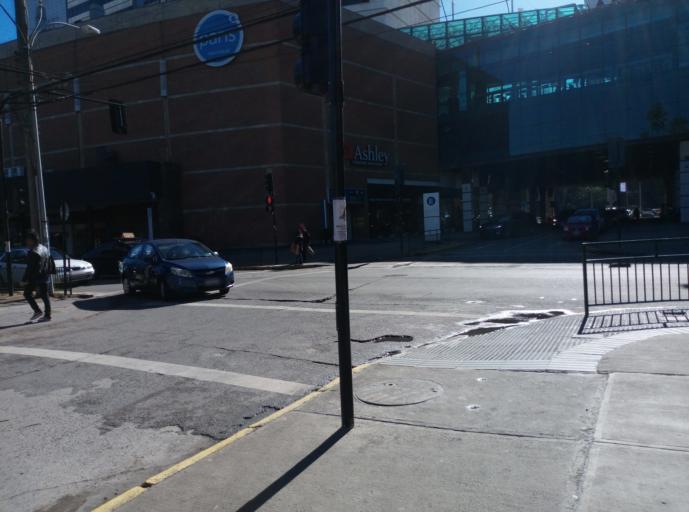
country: CL
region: Valparaiso
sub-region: Provincia de Valparaiso
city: Vina del Mar
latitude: -33.0095
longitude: -71.5474
